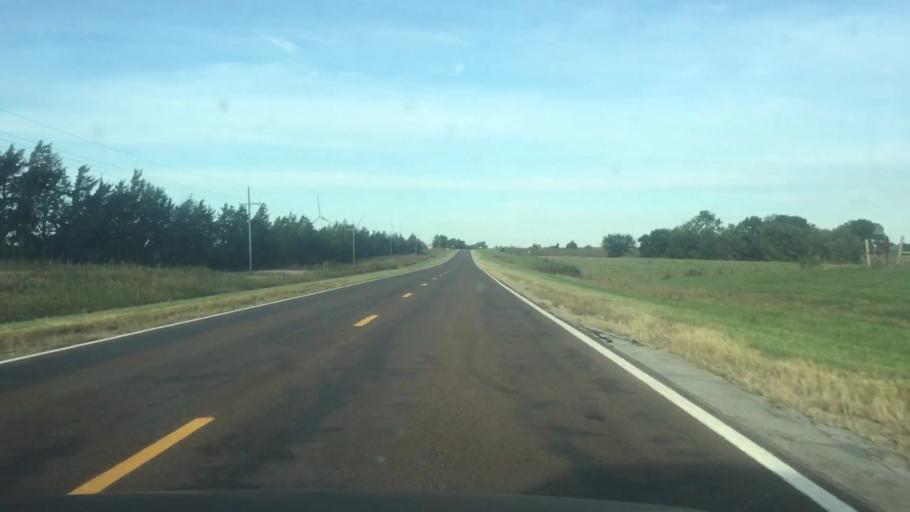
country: US
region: Nebraska
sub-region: Gage County
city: Wymore
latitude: 40.0449
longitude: -96.8698
